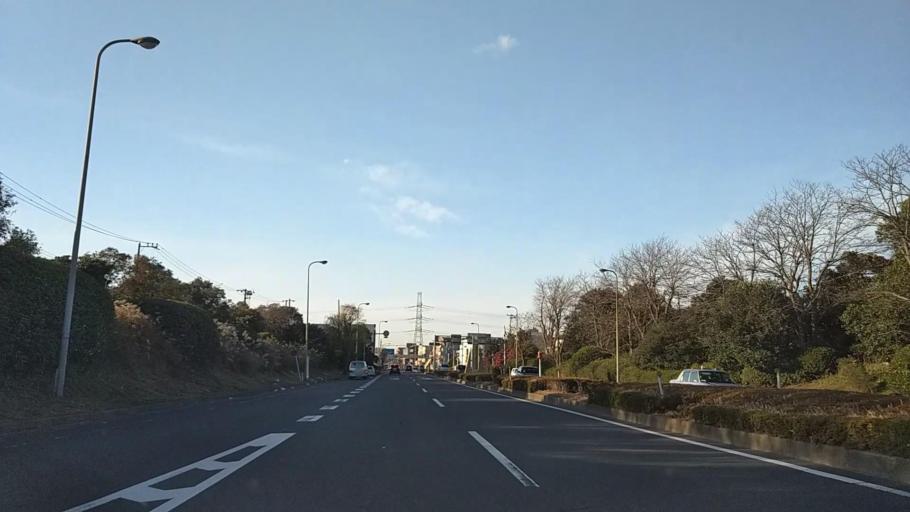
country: JP
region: Tokyo
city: Urayasu
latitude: 35.6565
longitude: 139.9071
